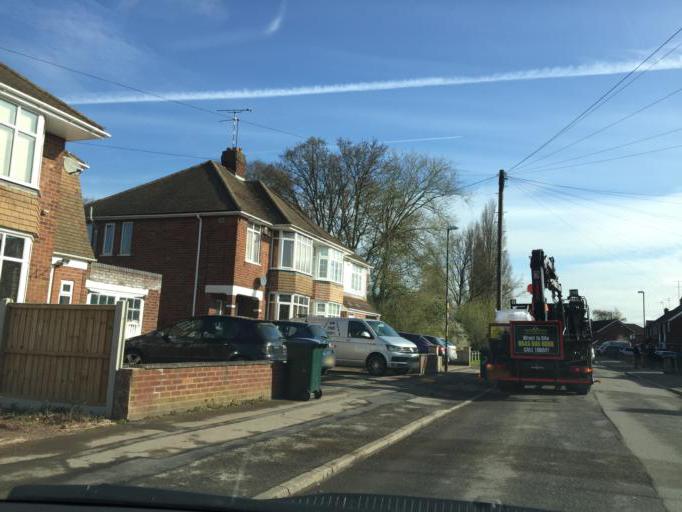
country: GB
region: England
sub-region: Coventry
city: Coventry
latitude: 52.3820
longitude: -1.5073
